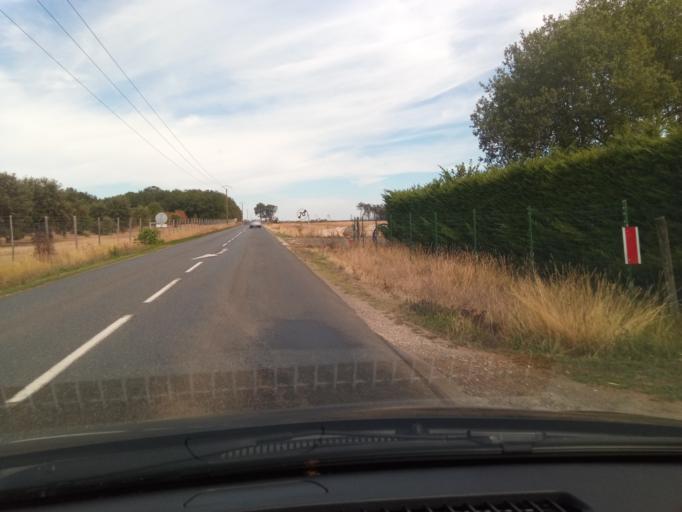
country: FR
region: Poitou-Charentes
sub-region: Departement de la Vienne
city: Chauvigny
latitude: 46.5498
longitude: 0.6022
